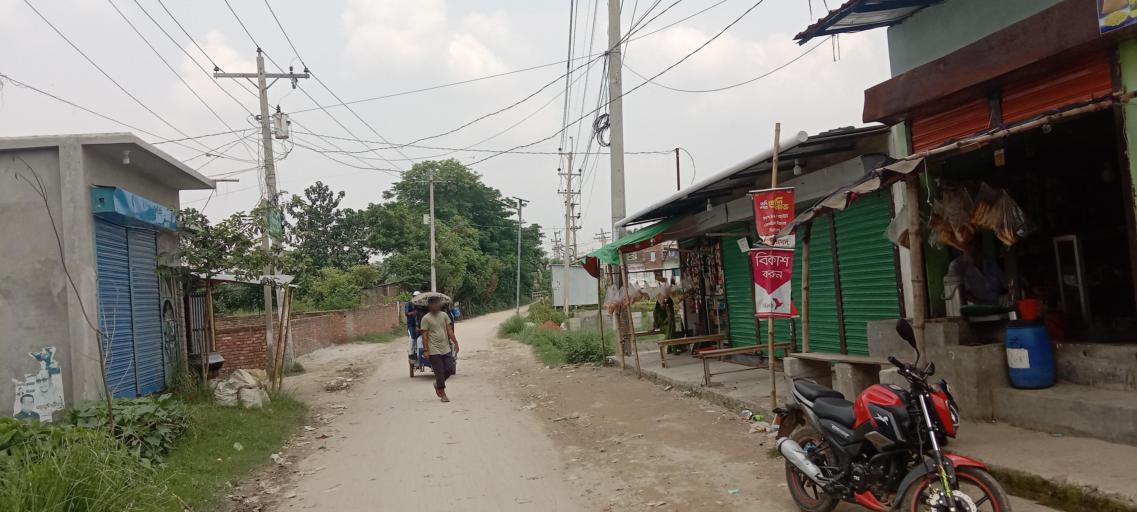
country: BD
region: Dhaka
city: Azimpur
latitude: 23.7062
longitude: 90.3526
